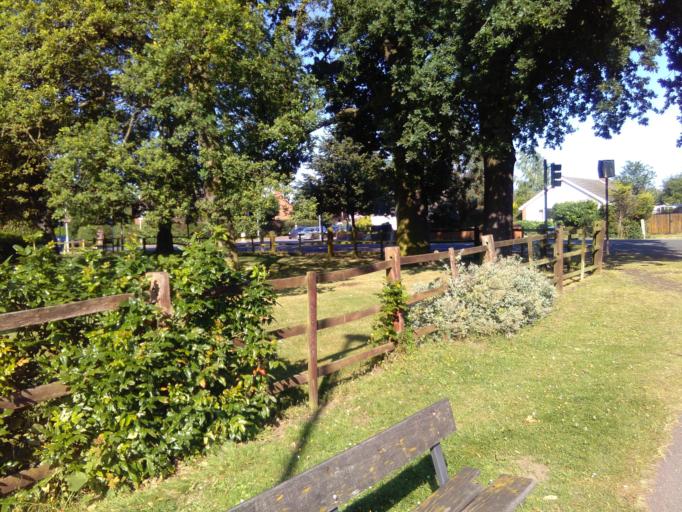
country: GB
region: England
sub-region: Bedford
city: Bedford
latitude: 52.1494
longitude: -0.4546
